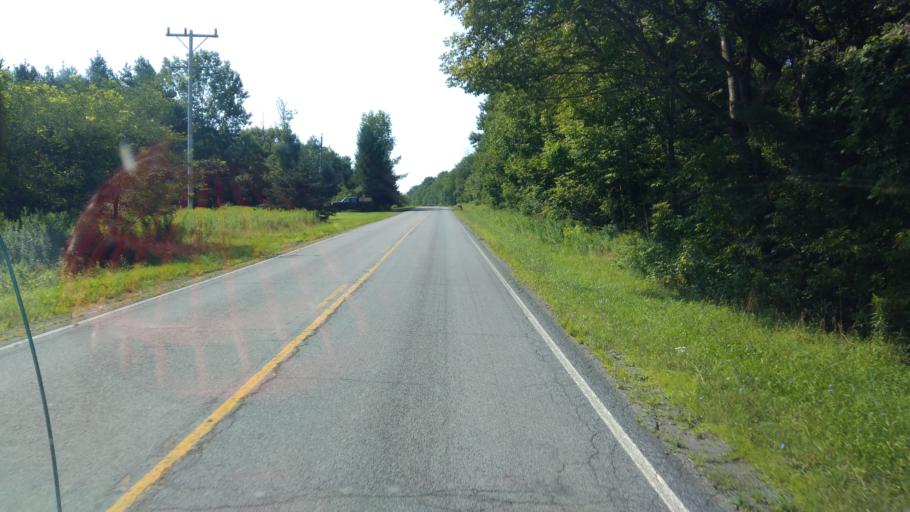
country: US
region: New York
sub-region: Allegany County
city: Friendship
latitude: 42.1467
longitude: -78.1498
